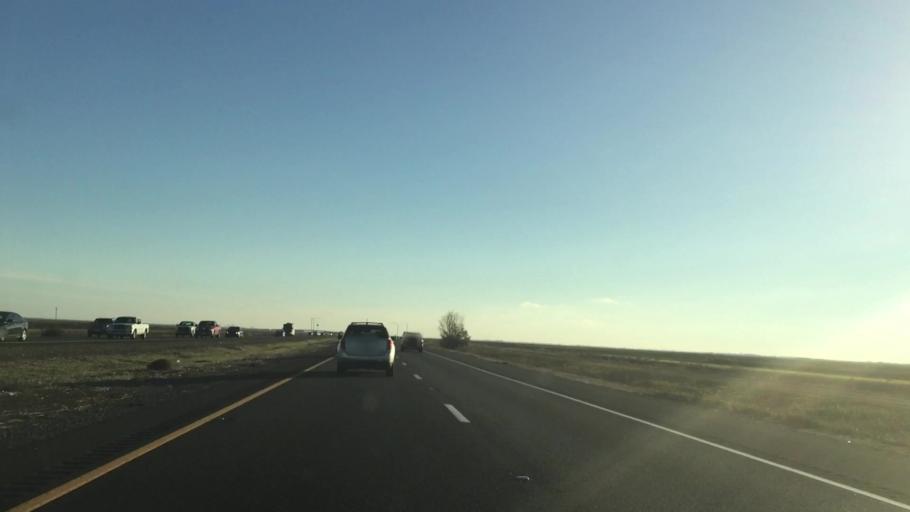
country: US
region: California
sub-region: Sacramento County
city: Elverta
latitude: 38.7854
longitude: -121.5438
